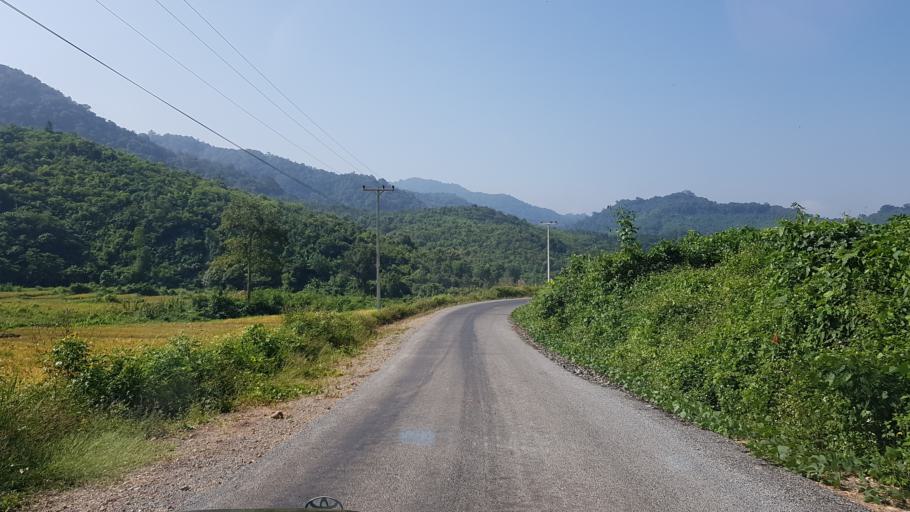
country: LA
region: Oudomxai
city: Muang Xay
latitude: 20.7127
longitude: 102.0637
